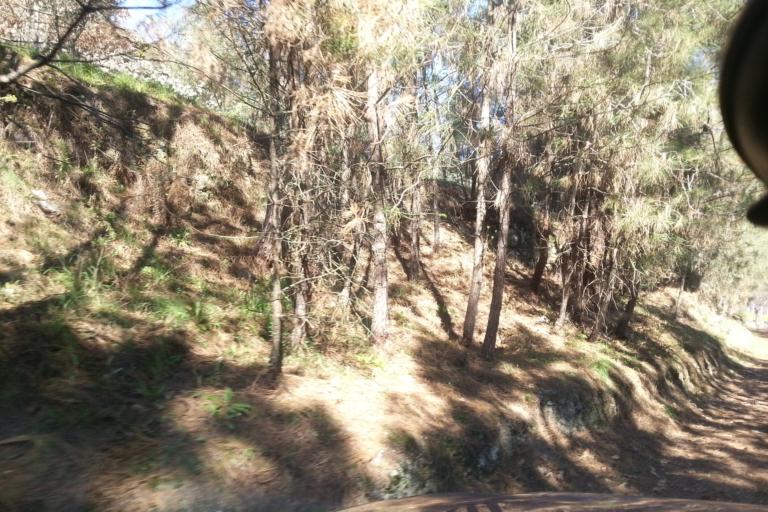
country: PT
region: Guarda
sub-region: Fornos de Algodres
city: Fornos de Algodres
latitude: 40.6264
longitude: -7.5367
